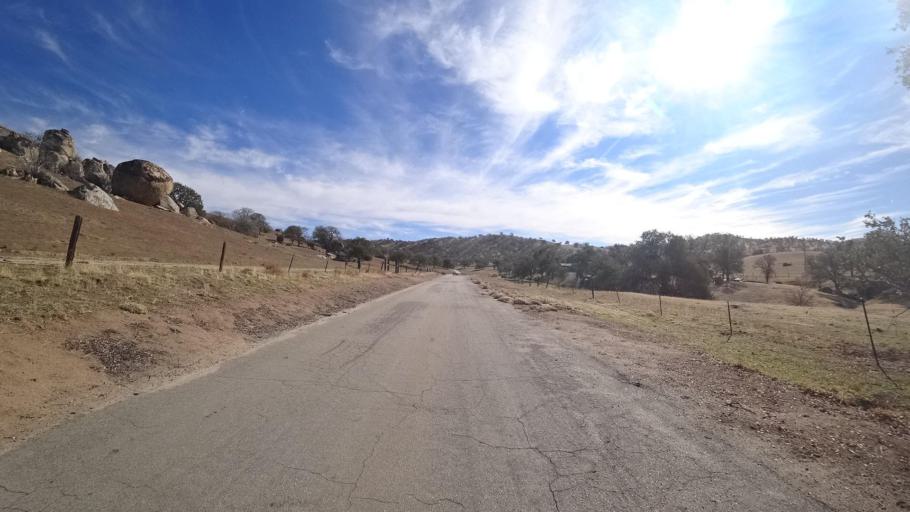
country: US
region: California
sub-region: Kern County
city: Oildale
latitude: 35.5816
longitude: -118.8155
